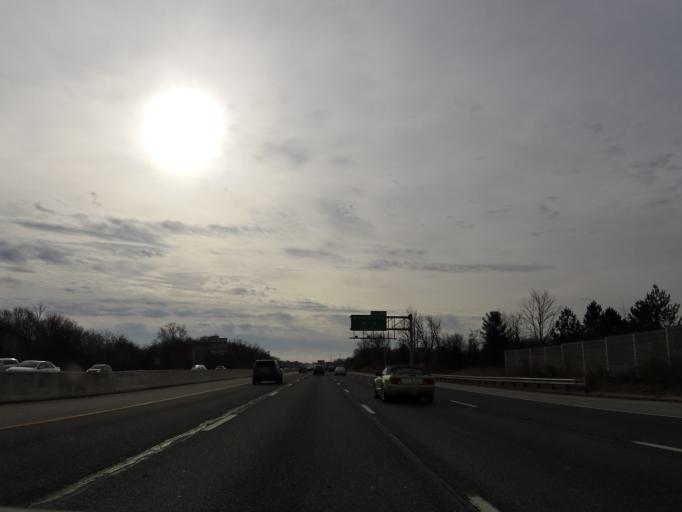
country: US
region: Indiana
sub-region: Marion County
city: Lawrence
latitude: 39.8757
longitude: -86.0474
